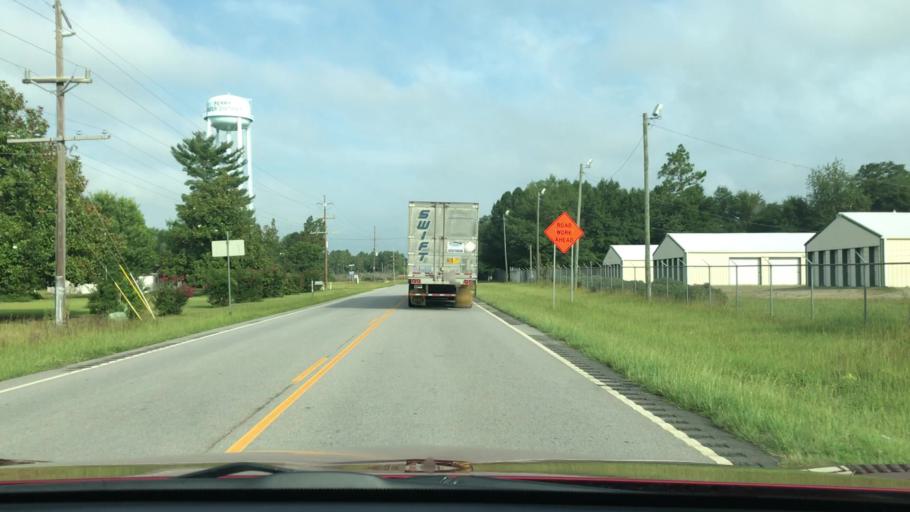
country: US
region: South Carolina
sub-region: Barnwell County
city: Williston
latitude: 33.6381
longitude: -81.3278
